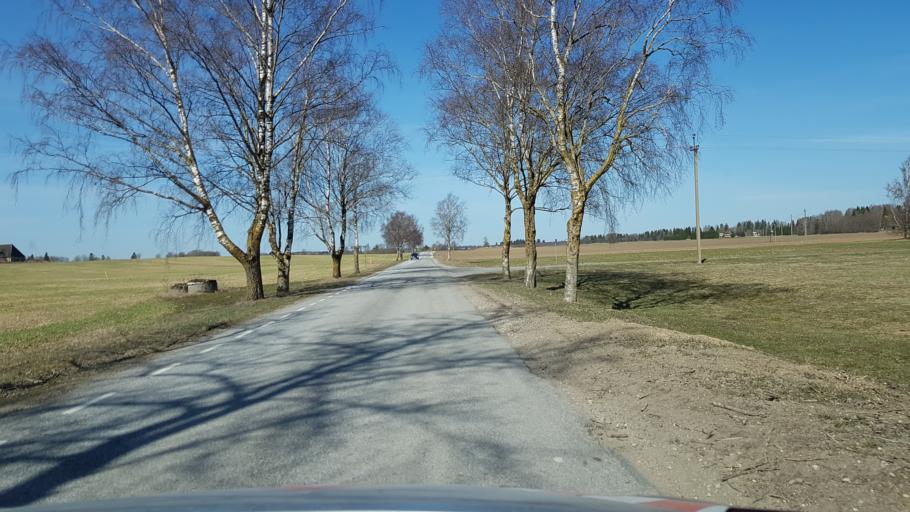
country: EE
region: Laeaene-Virumaa
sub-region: Vinni vald
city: Vinni
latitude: 59.2963
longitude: 26.4230
